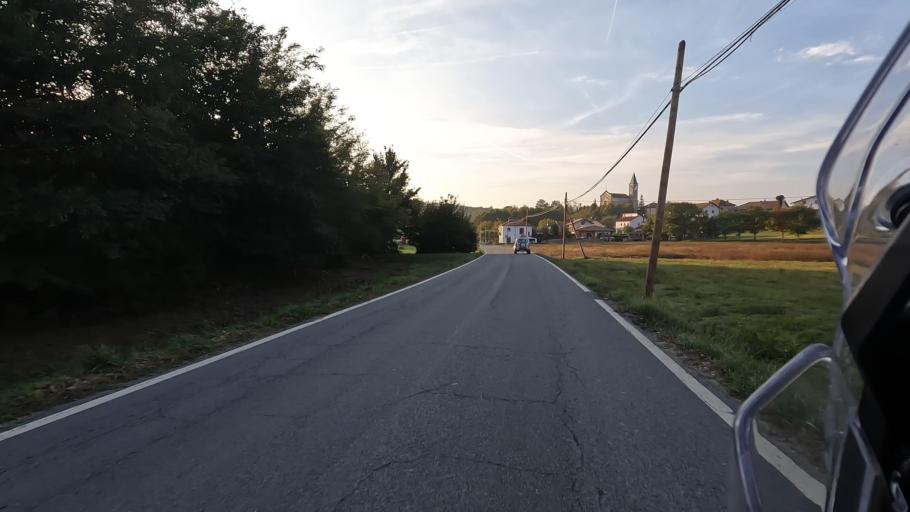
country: IT
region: Liguria
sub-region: Provincia di Savona
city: Sassello
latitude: 44.4996
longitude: 8.4914
